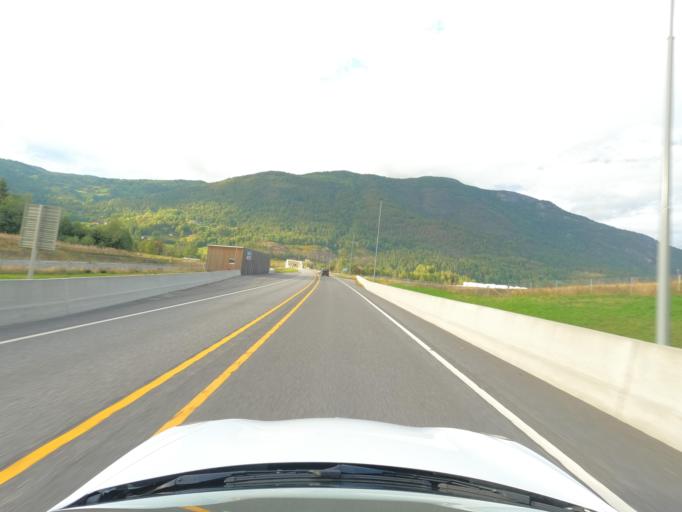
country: NO
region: Telemark
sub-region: Seljord
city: Seljord
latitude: 59.5975
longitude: 8.7153
